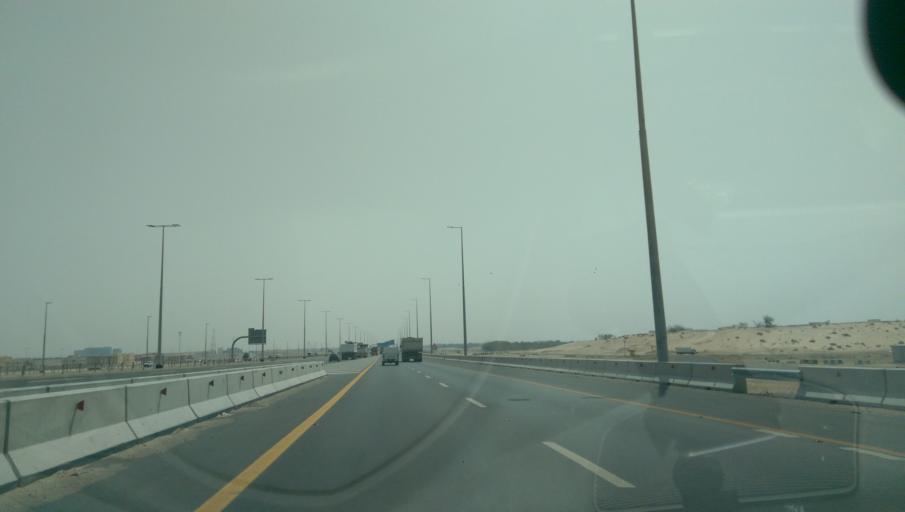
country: AE
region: Abu Dhabi
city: Abu Dhabi
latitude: 24.2980
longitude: 54.5832
